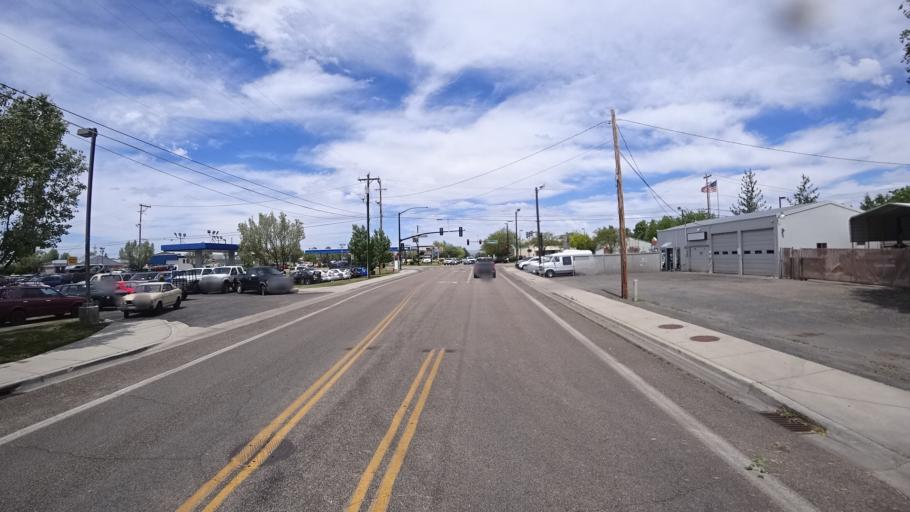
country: US
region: Idaho
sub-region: Ada County
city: Garden City
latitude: 43.6186
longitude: -116.3042
